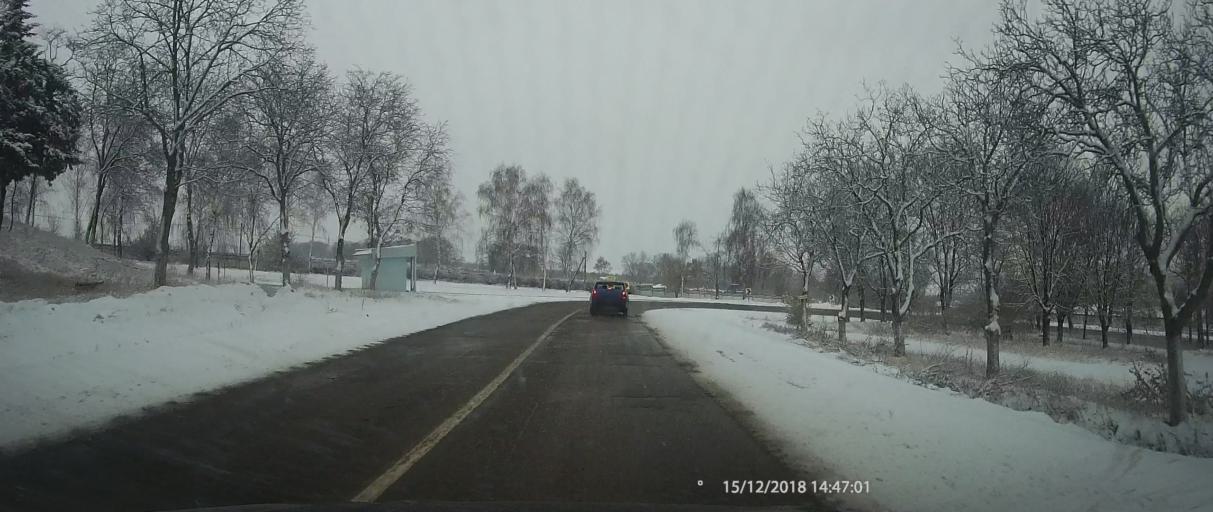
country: MD
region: Cahul
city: Cahul
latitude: 45.8913
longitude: 28.2095
